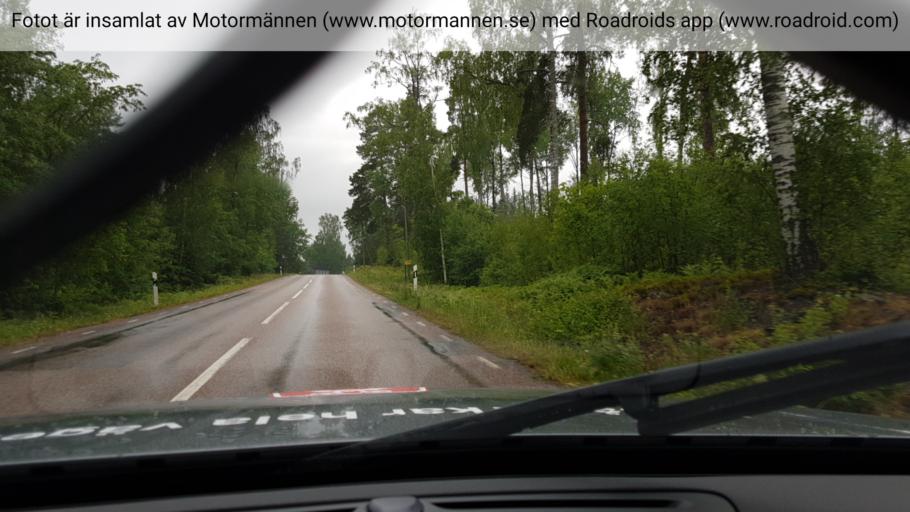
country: SE
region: Vaestmanland
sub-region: Norbergs Kommun
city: Norberg
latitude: 60.0233
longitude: 16.0136
